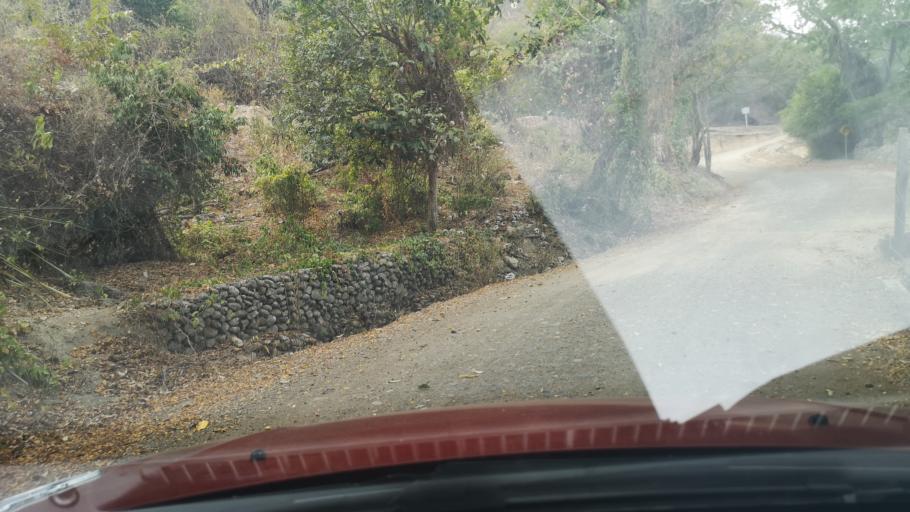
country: CO
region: Huila
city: Neiva
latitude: 2.9573
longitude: -75.3498
